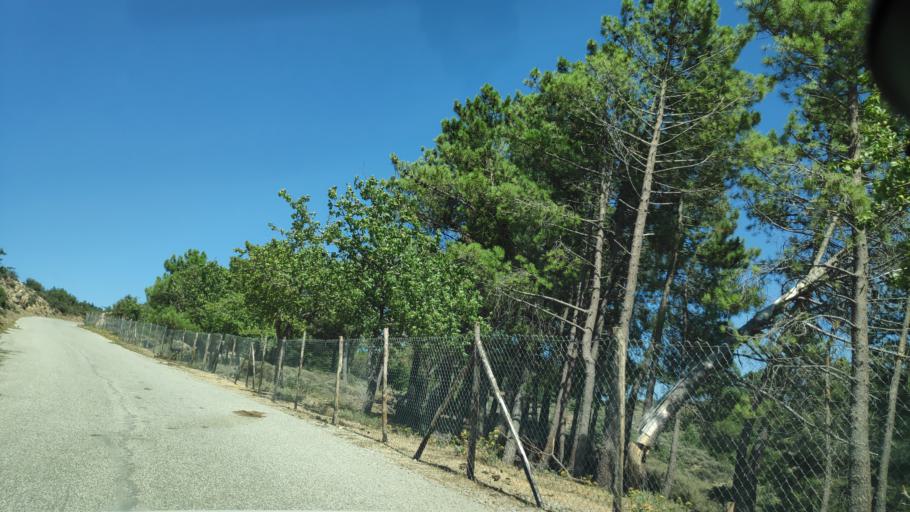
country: IT
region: Calabria
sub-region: Provincia di Reggio Calabria
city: Bova
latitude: 38.0209
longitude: 15.9371
